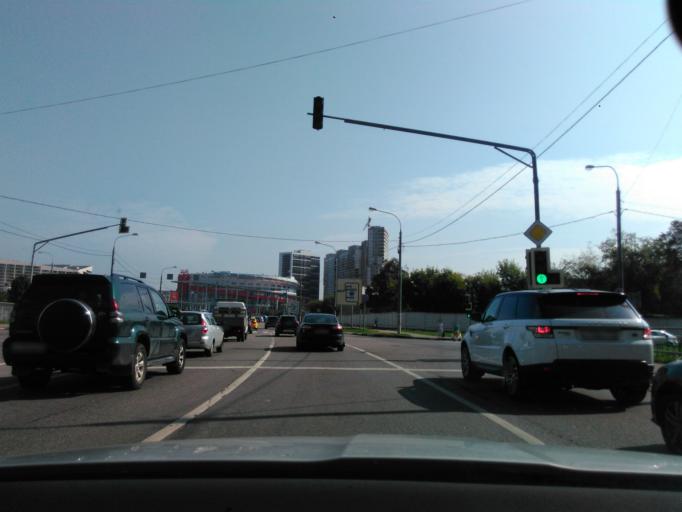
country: RU
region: Moscow
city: Sokol
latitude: 55.7824
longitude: 37.5335
